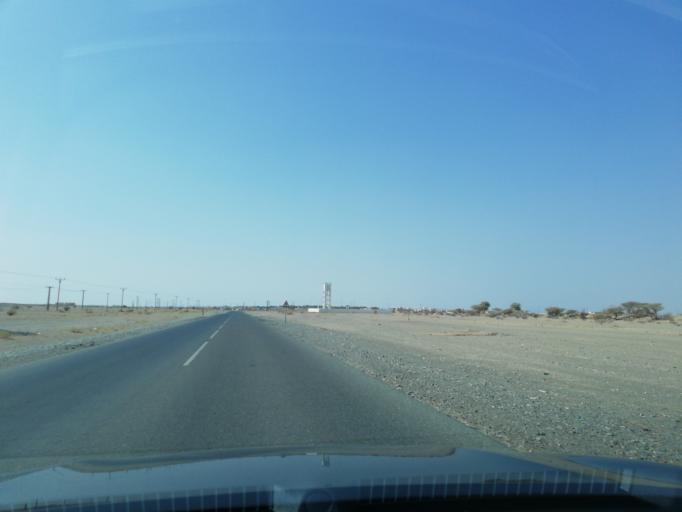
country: OM
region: Muhafazat ad Dakhiliyah
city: Adam
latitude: 22.3161
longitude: 58.0671
